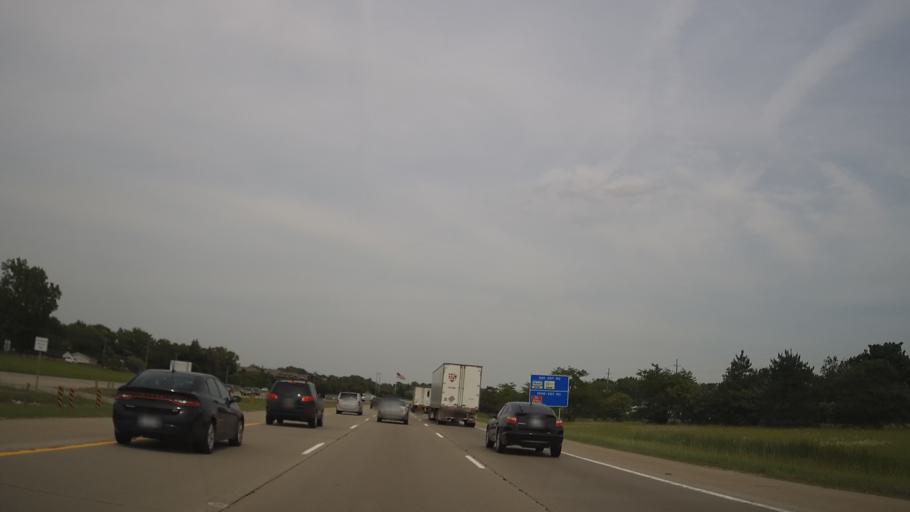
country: US
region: Michigan
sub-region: Wayne County
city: Belleville
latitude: 42.2207
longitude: -83.4528
